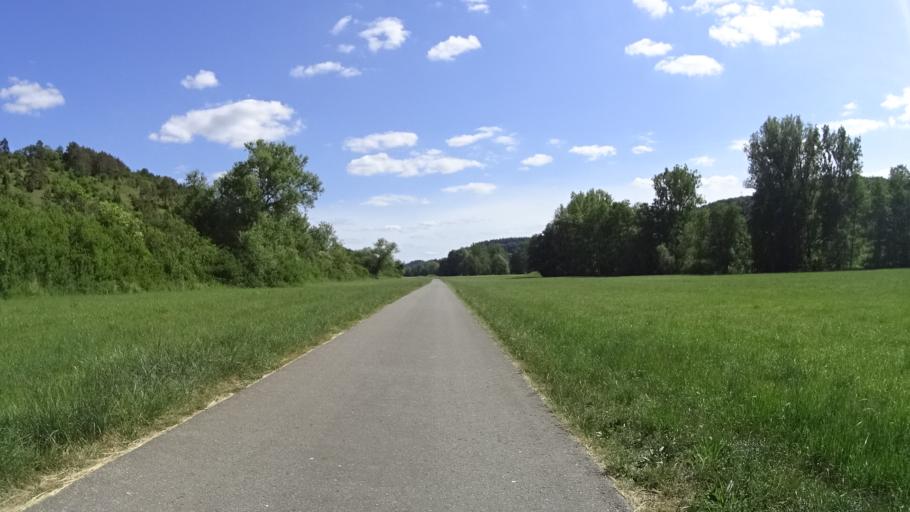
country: DE
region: Baden-Wuerttemberg
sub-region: Karlsruhe Region
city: Hardheim
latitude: 49.5998
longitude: 9.4783
